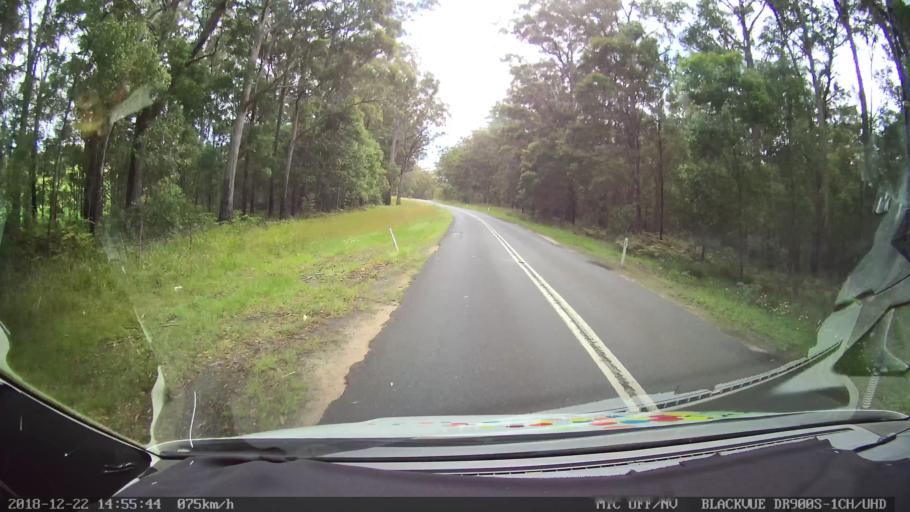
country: AU
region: New South Wales
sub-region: Bellingen
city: Dorrigo
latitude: -30.2309
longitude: 152.5182
